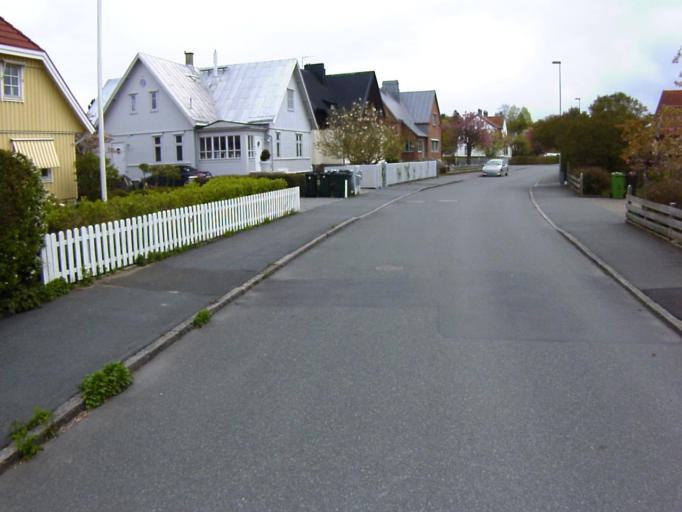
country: SE
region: Skane
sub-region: Kristianstads Kommun
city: Kristianstad
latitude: 56.0372
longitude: 14.1709
